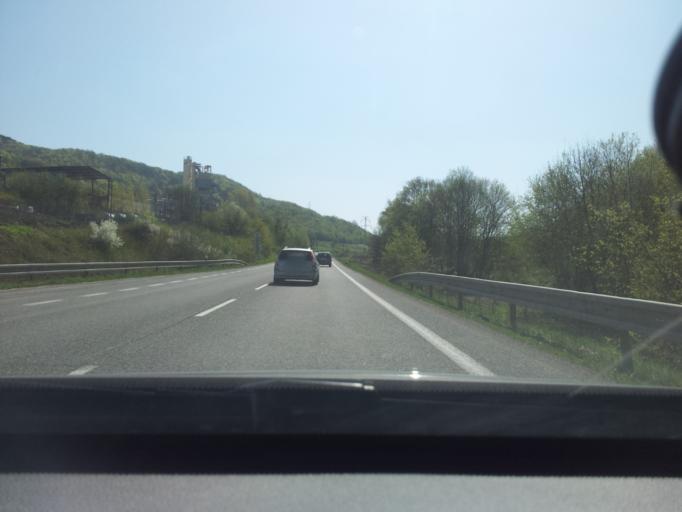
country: SK
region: Trenciansky
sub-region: Okres Trencin
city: Trencin
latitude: 48.8255
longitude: 18.0675
